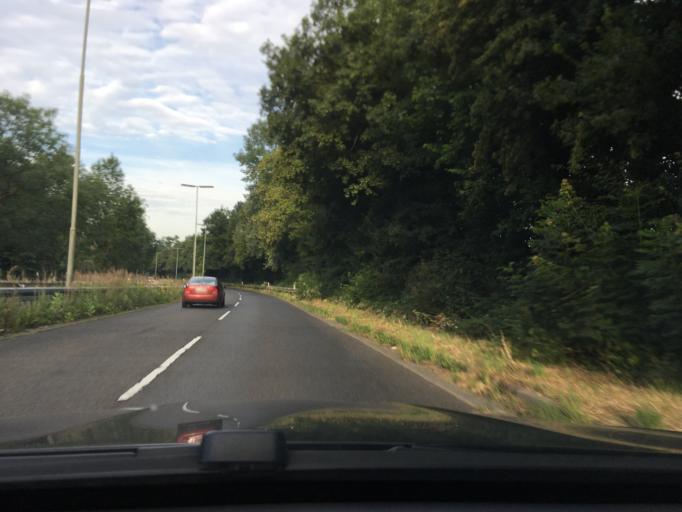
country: DE
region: North Rhine-Westphalia
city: Opladen
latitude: 51.0422
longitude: 7.0572
